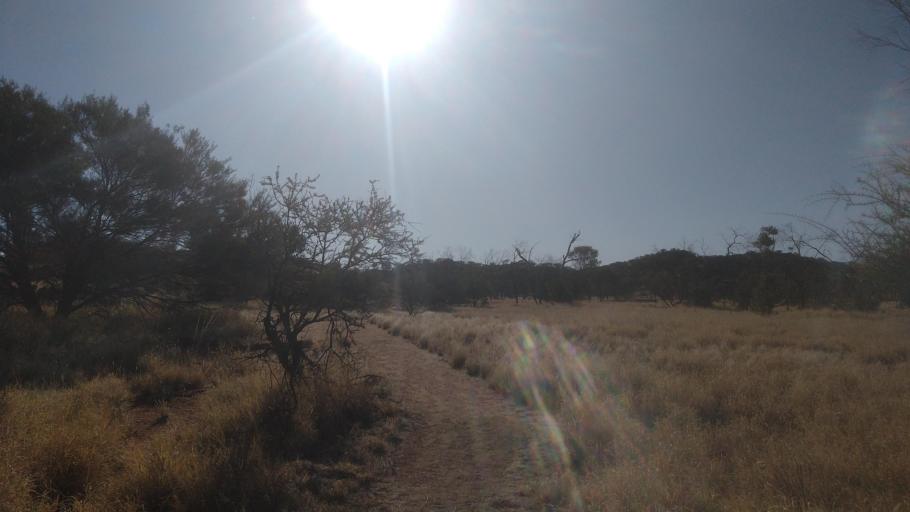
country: AU
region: Northern Territory
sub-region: Alice Springs
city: Alice Springs
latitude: -23.6697
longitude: 133.8842
